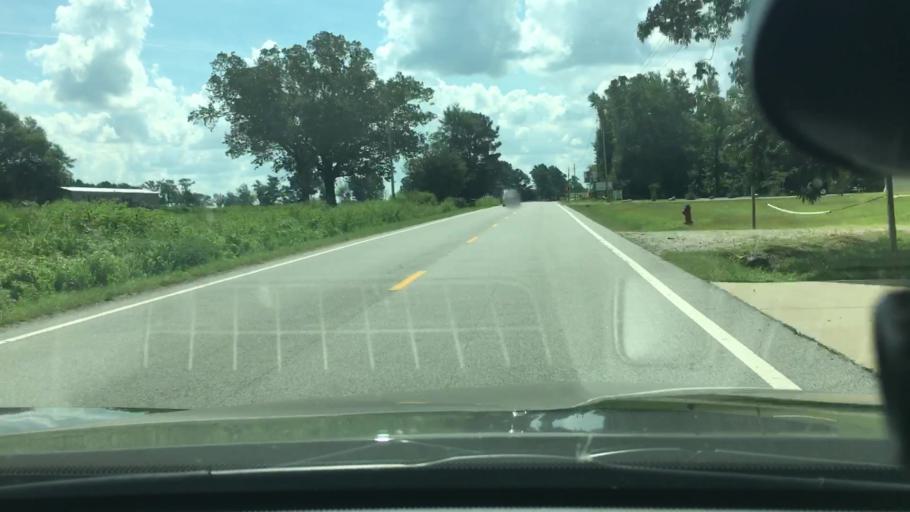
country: US
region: North Carolina
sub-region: Pitt County
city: Farmville
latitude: 35.6843
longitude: -77.4926
